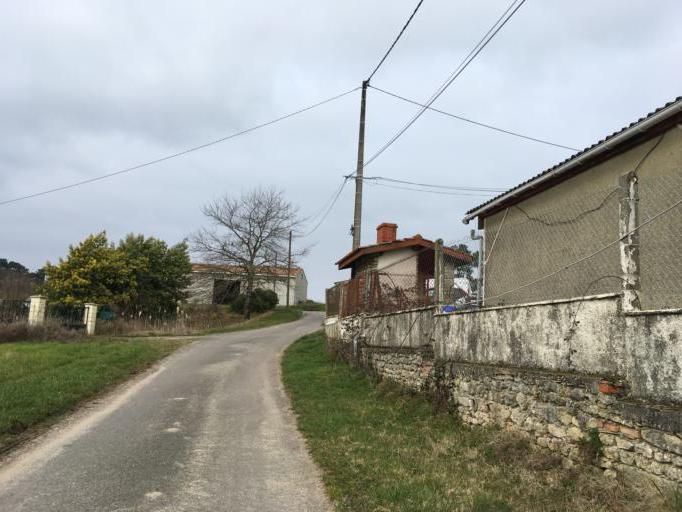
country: FR
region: Poitou-Charentes
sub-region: Departement de la Charente-Maritime
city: Mirambeau
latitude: 45.3345
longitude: -0.5930
